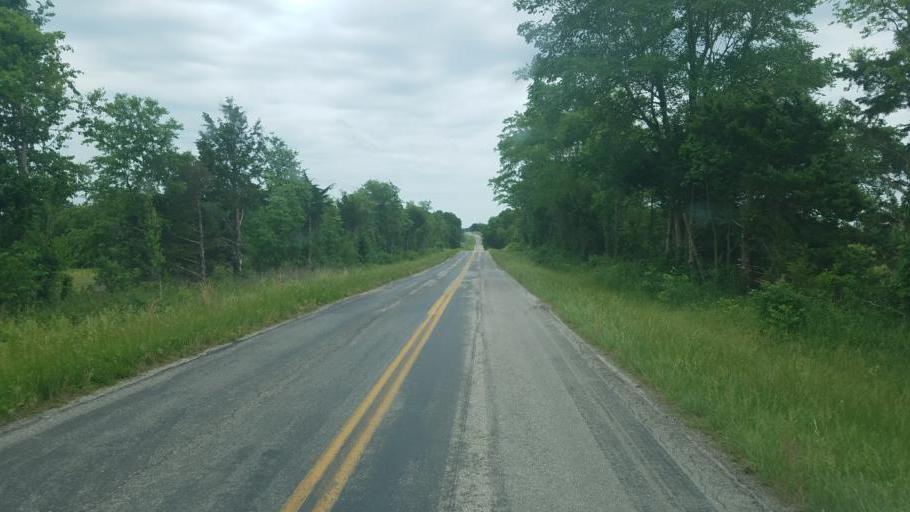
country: US
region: Missouri
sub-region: Moniteau County
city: Tipton
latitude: 38.5660
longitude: -92.7172
